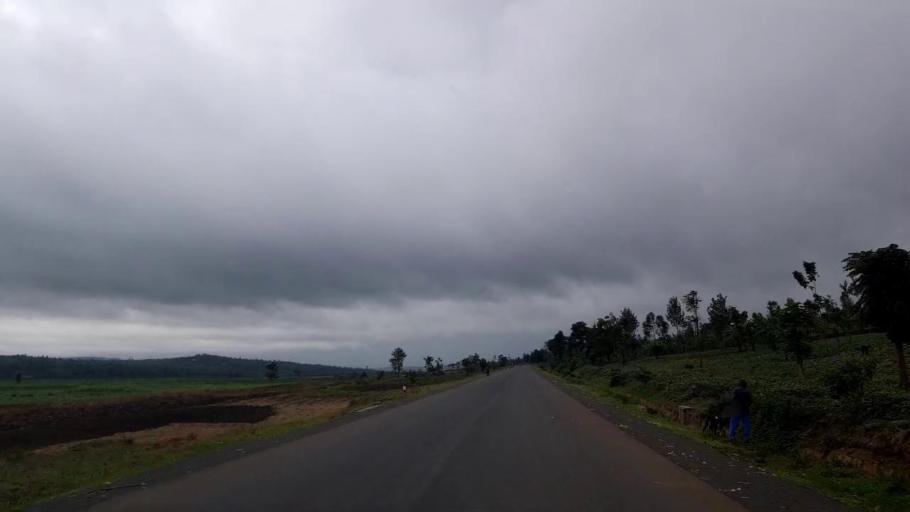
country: RW
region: Northern Province
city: Byumba
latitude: -1.4419
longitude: 30.2532
